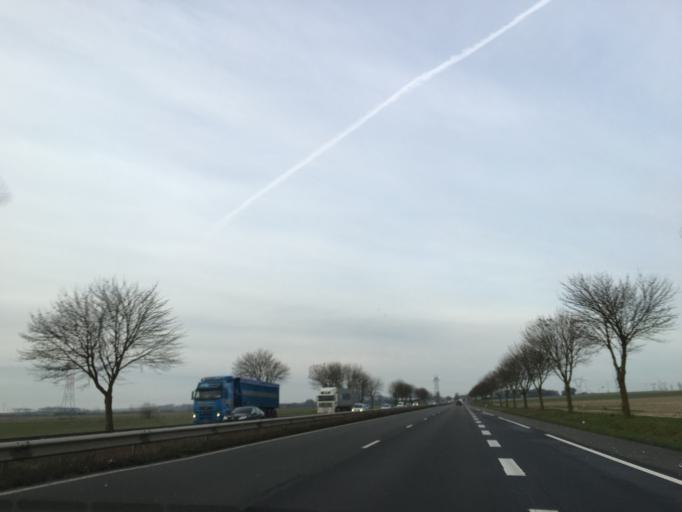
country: FR
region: Nord-Pas-de-Calais
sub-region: Departement du Pas-de-Calais
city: Roeux
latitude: 50.3332
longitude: 2.9115
